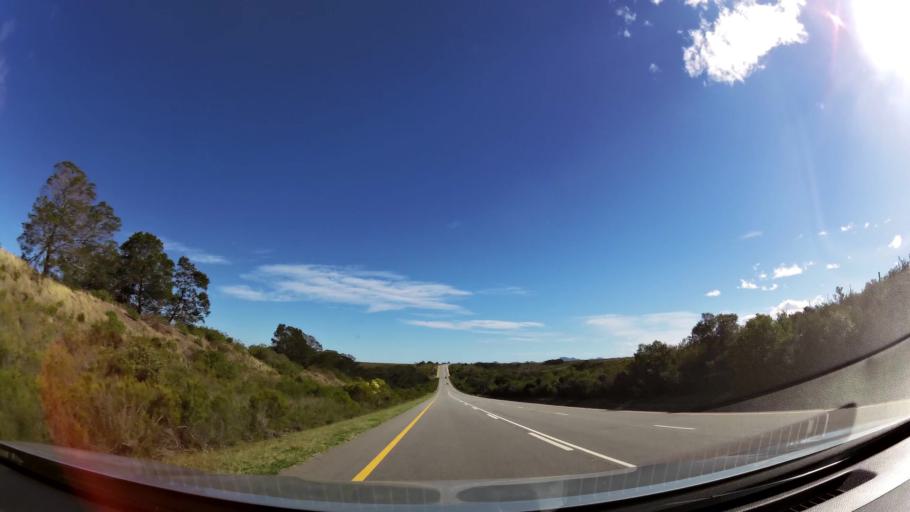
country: ZA
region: Eastern Cape
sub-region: Cacadu District Municipality
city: Kruisfontein
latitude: -34.0063
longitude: 24.6722
